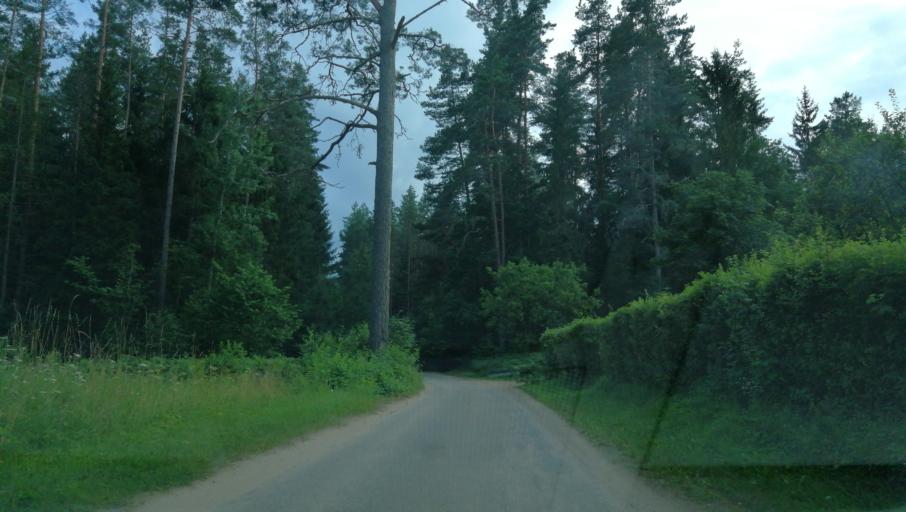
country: LV
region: Cesu Rajons
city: Cesis
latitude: 57.3111
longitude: 25.2195
